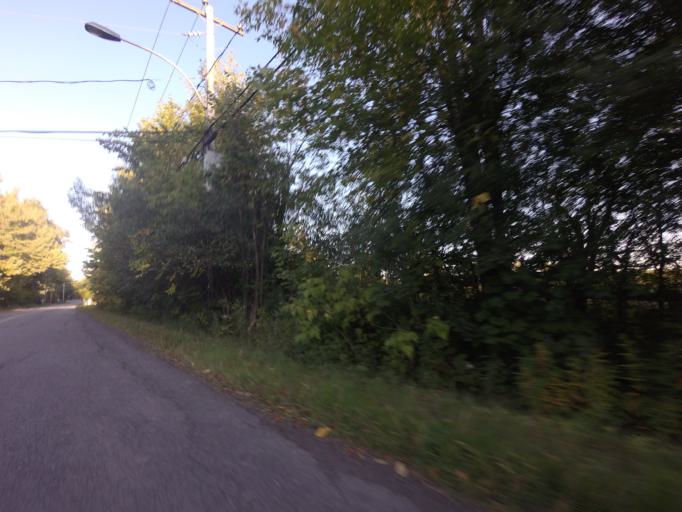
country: CA
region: Quebec
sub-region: Monteregie
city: Hudson
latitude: 45.4822
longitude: -74.2179
